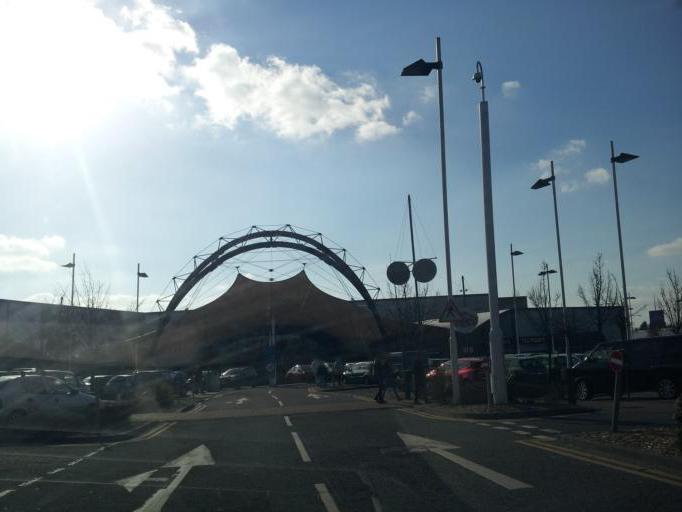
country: GB
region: England
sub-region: South Gloucestershire
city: Almondsbury
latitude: 51.5237
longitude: -2.6029
